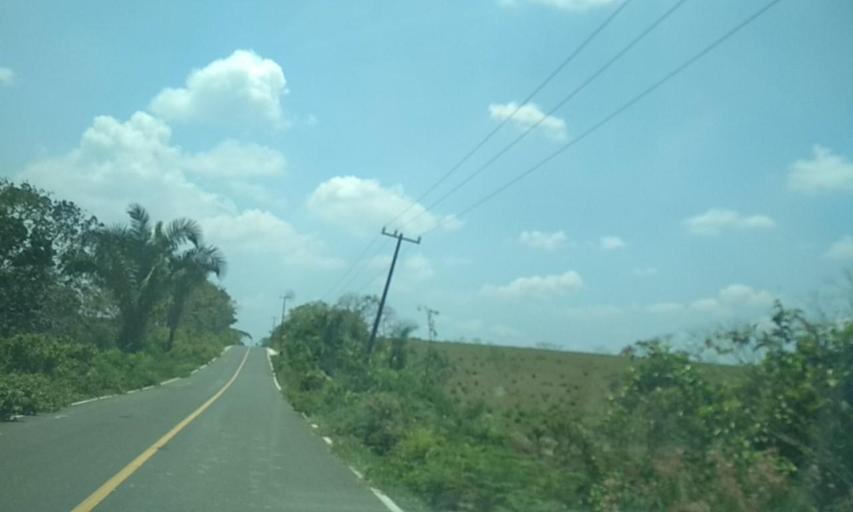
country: MX
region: Tabasco
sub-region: Huimanguillo
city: Francisco Rueda
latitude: 17.7627
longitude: -94.0588
